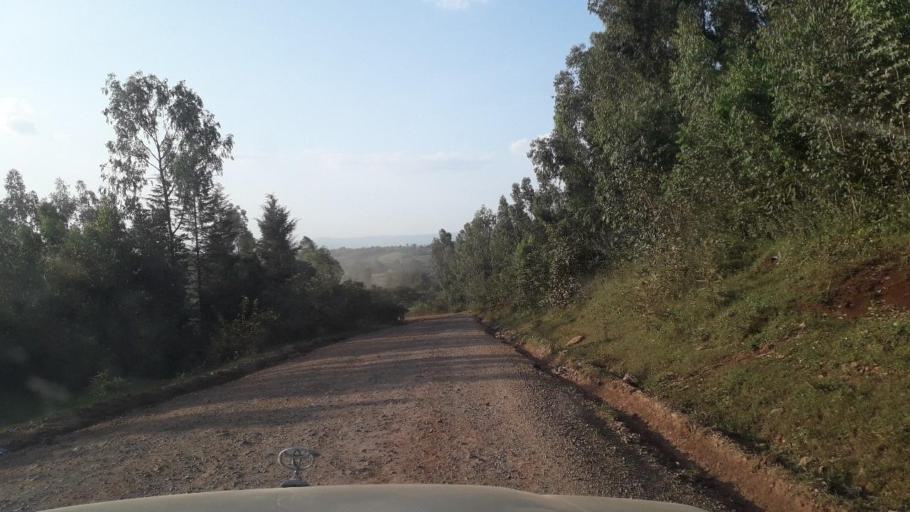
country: ET
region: Oromiya
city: Jima
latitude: 7.5722
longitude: 36.8600
